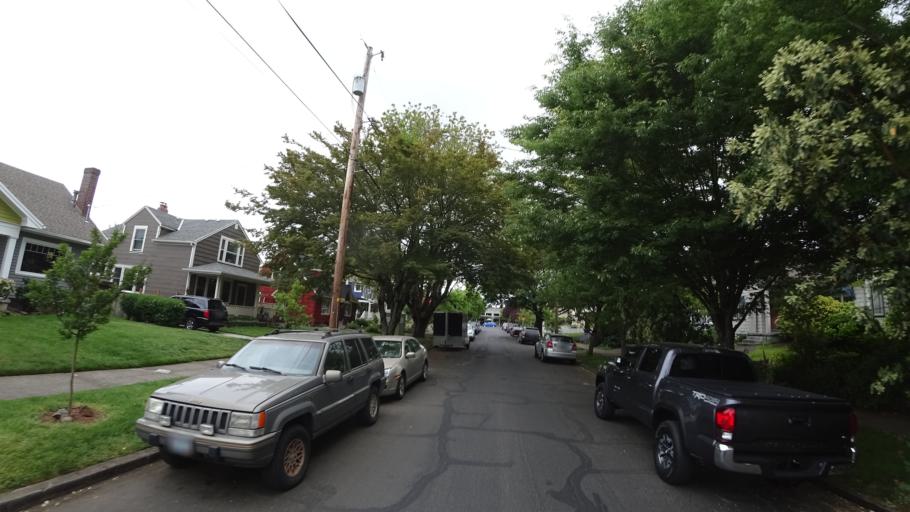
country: US
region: Oregon
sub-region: Multnomah County
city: Portland
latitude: 45.5473
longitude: -122.6188
